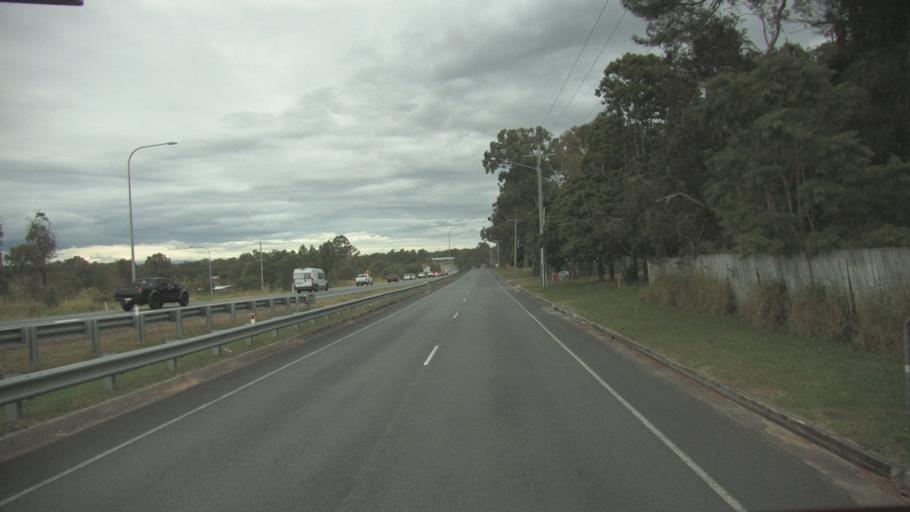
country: AU
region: Queensland
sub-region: Logan
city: Park Ridge South
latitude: -27.7182
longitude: 153.0323
